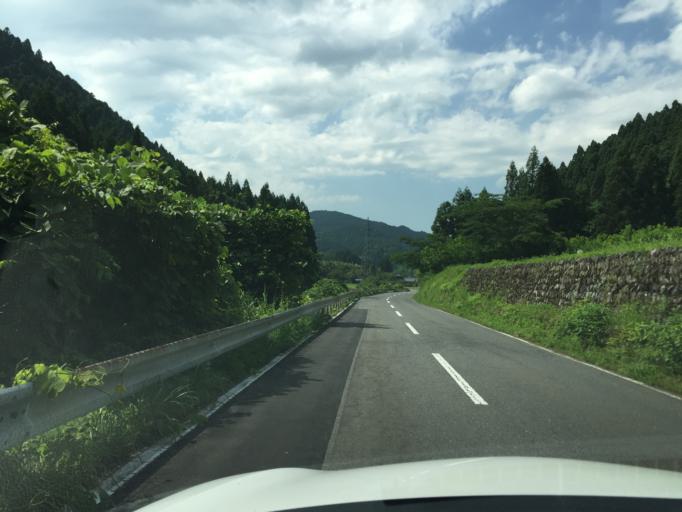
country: JP
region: Fukushima
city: Iwaki
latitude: 37.0111
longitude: 140.7083
